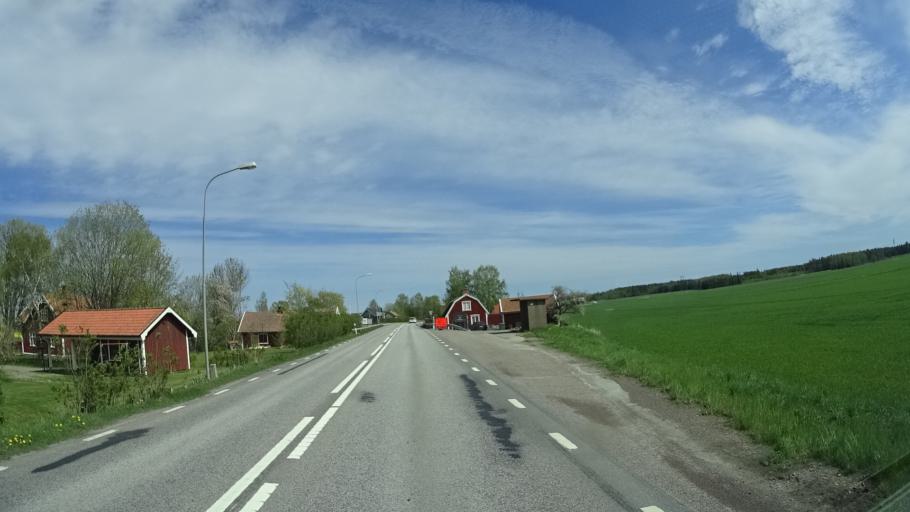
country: SE
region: OEstergoetland
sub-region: Mjolby Kommun
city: Mantorp
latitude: 58.3671
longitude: 15.3147
